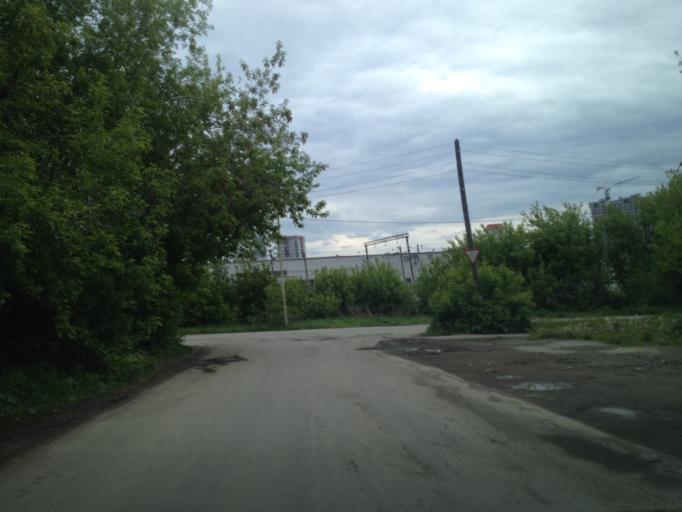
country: RU
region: Sverdlovsk
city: Yekaterinburg
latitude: 56.8606
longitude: 60.5825
